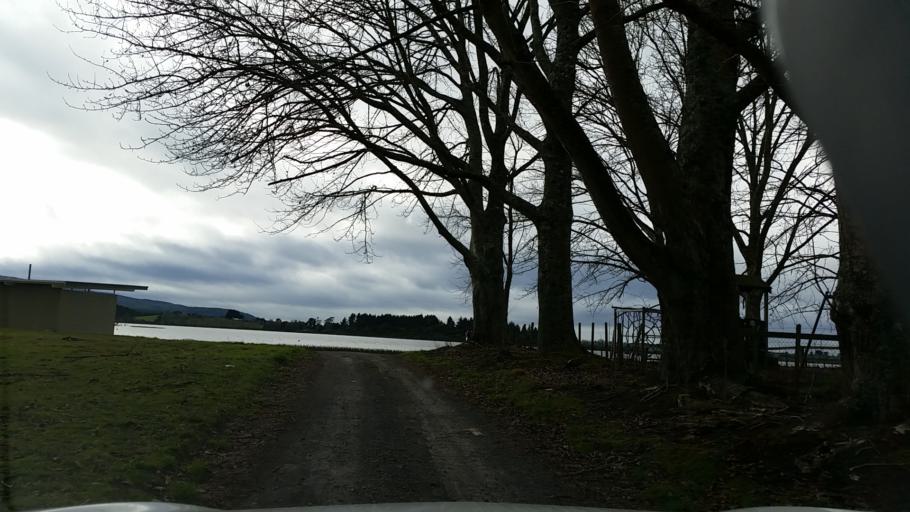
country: NZ
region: Bay of Plenty
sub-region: Whakatane District
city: Murupara
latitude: -38.3069
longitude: 176.5010
